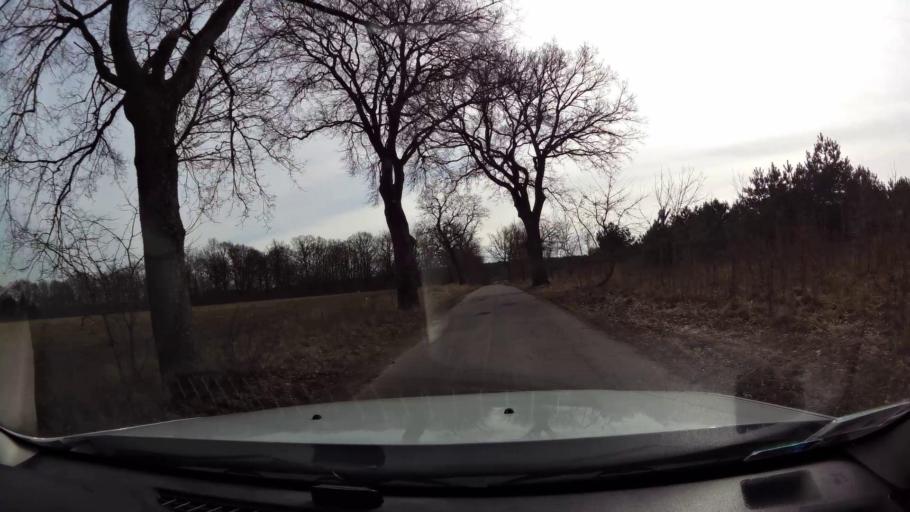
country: PL
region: West Pomeranian Voivodeship
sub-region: Powiat stargardzki
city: Insko
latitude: 53.4473
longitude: 15.6419
